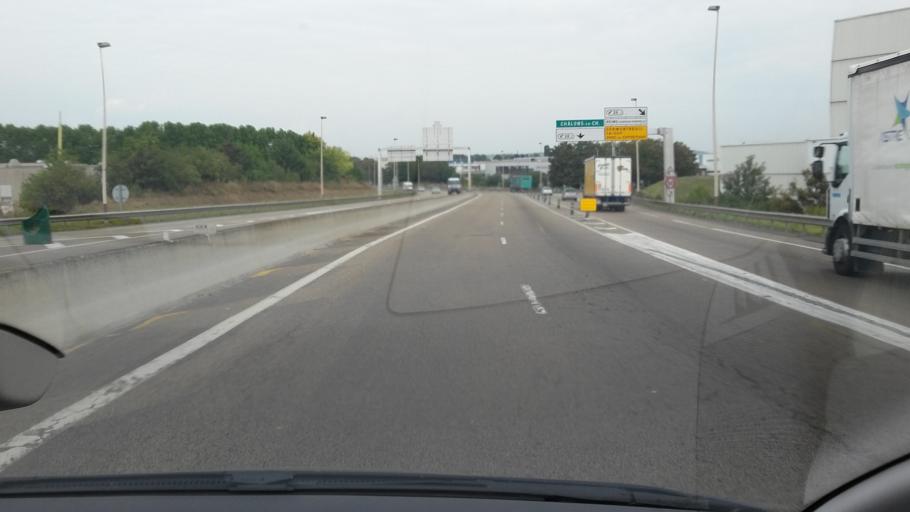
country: FR
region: Champagne-Ardenne
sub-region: Departement de la Marne
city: Cormontreuil
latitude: 49.2308
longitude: 4.0696
